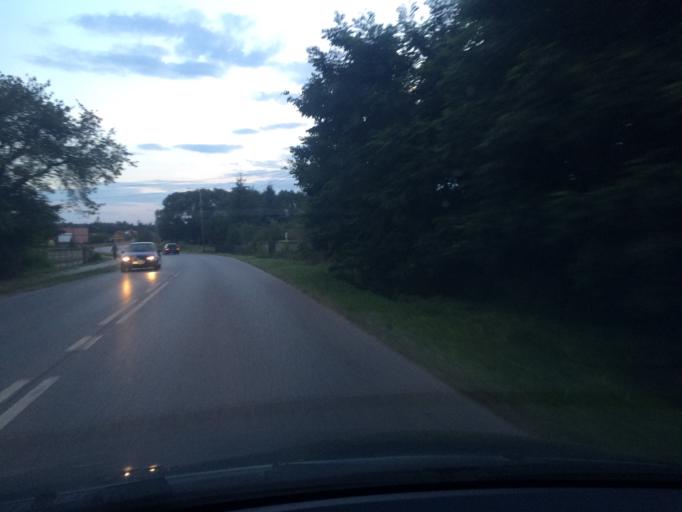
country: PL
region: Swietokrzyskie
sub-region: Powiat skarzyski
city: Suchedniow
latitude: 51.0468
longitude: 20.8870
